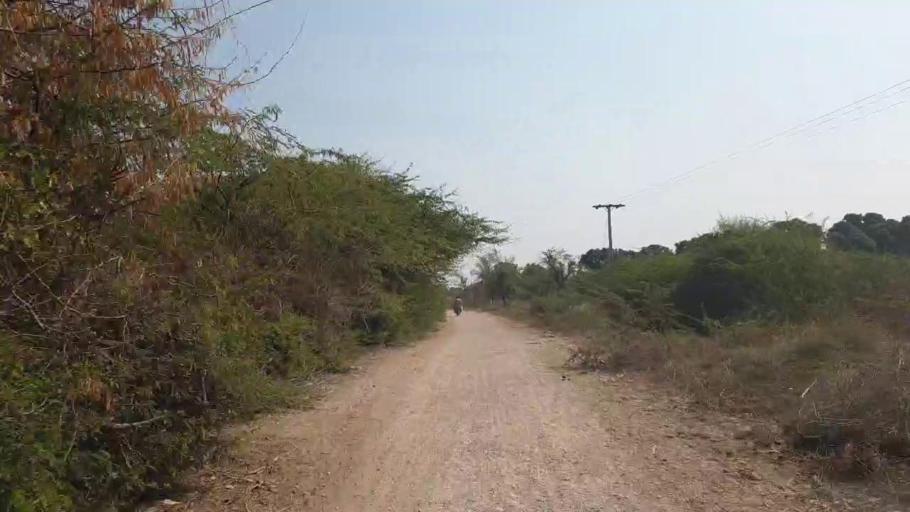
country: PK
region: Sindh
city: Chambar
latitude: 25.4093
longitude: 68.9034
